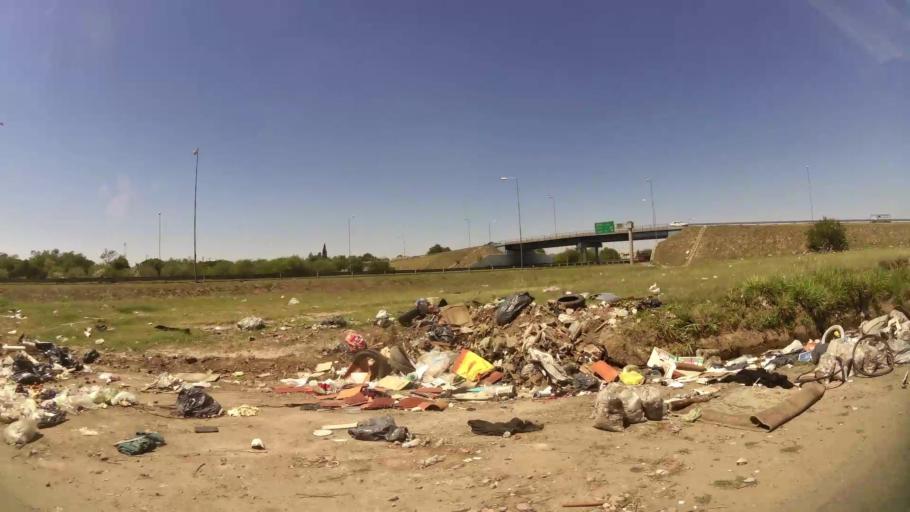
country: AR
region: Cordoba
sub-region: Departamento de Capital
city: Cordoba
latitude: -31.4390
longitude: -64.1208
